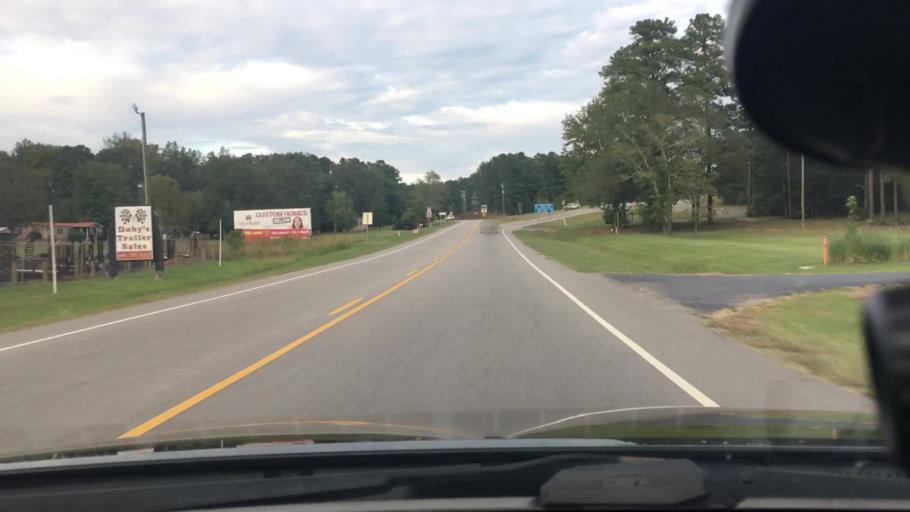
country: US
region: North Carolina
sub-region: Lee County
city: Sanford
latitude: 35.4022
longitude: -79.2347
